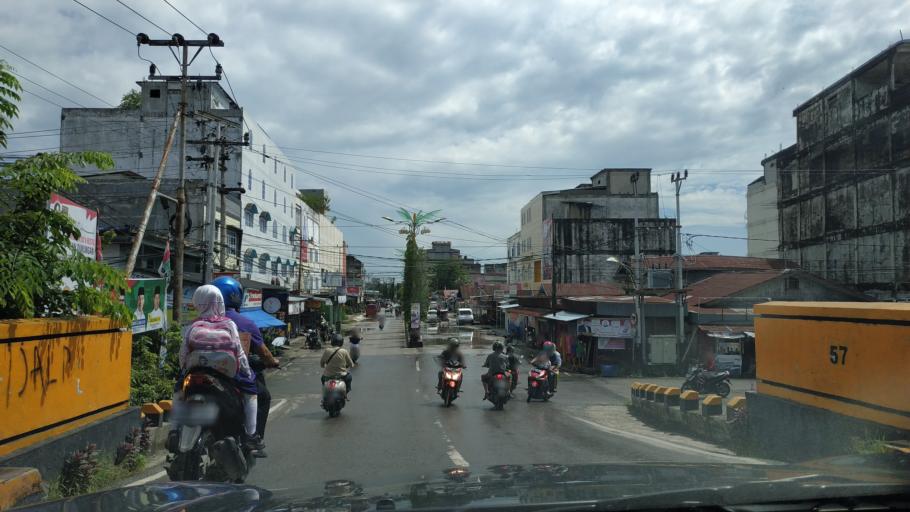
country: ID
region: Riau
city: Tembilahan
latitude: -0.3210
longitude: 103.1531
